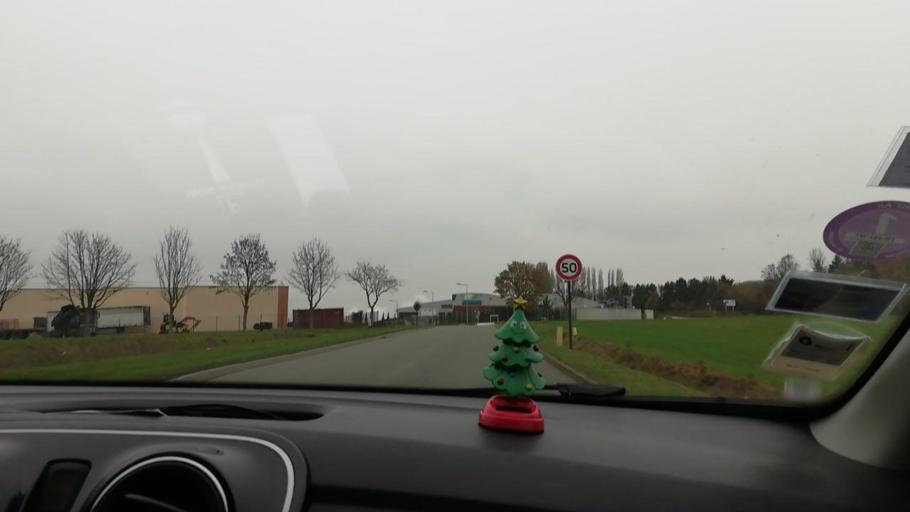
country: FR
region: Ile-de-France
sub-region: Departement de Seine-et-Marne
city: Saint-Soupplets
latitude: 49.0319
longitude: 2.7983
